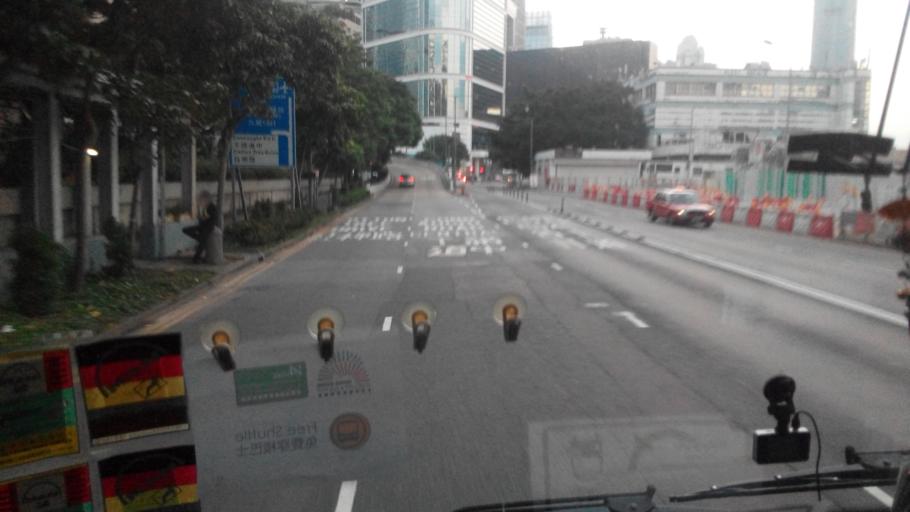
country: HK
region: Wanchai
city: Wan Chai
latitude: 22.2808
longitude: 114.1699
